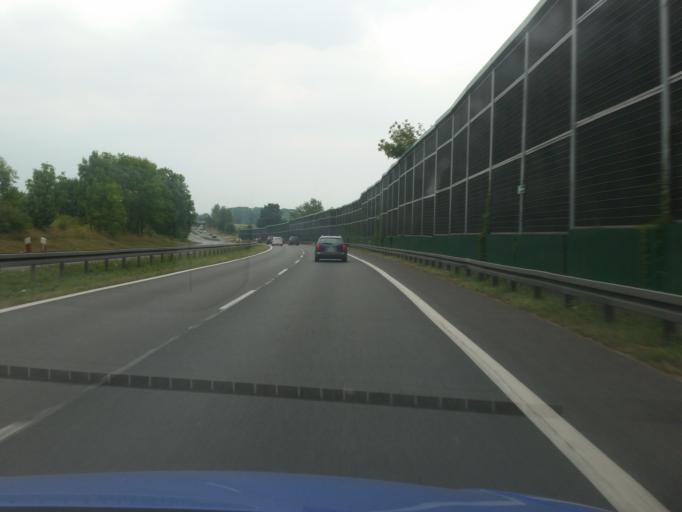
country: PL
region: Silesian Voivodeship
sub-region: Powiat bedzinski
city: Bedzin
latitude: 50.3331
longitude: 19.1100
